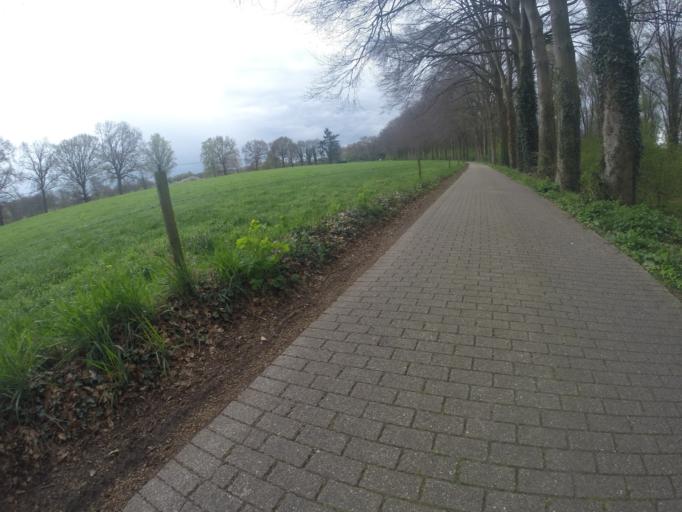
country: NL
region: Gelderland
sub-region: Gemeente Zutphen
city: Leesten
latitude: 52.1020
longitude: 6.2659
